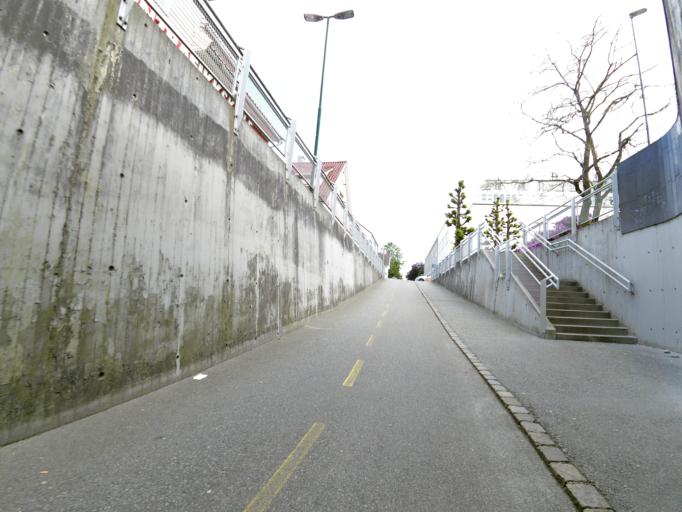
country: NO
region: Rogaland
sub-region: Stavanger
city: Stavanger
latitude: 58.9644
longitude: 5.7283
